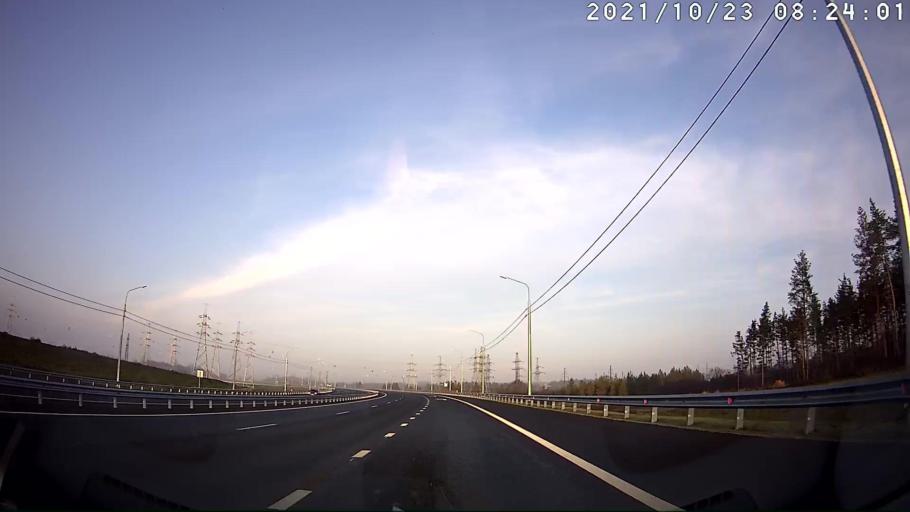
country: RU
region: Saratov
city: Sennoy
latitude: 52.1438
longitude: 46.9136
